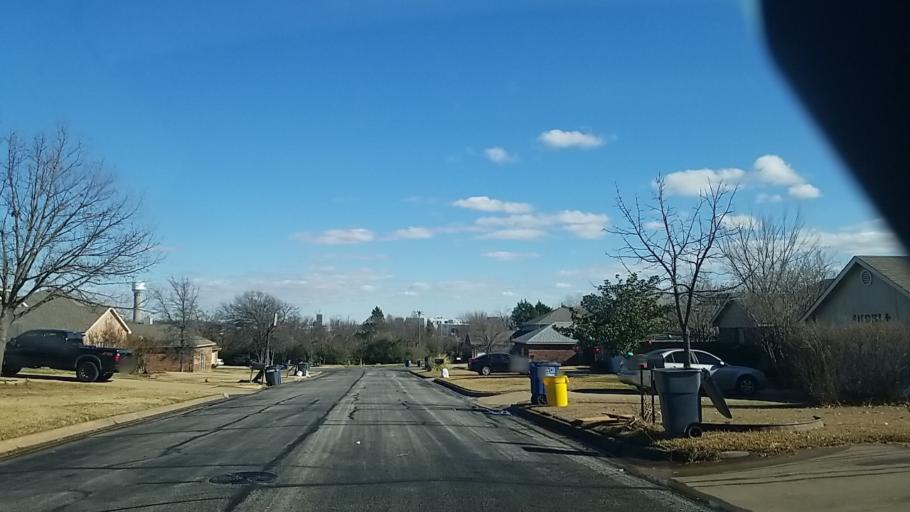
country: US
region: Texas
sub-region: Denton County
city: Corinth
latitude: 33.1571
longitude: -97.0715
